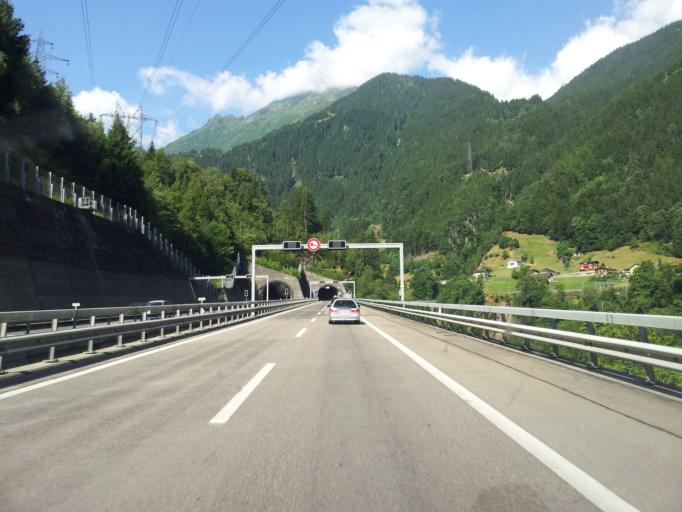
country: CH
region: Uri
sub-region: Uri
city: Silenen
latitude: 46.7593
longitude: 8.6543
